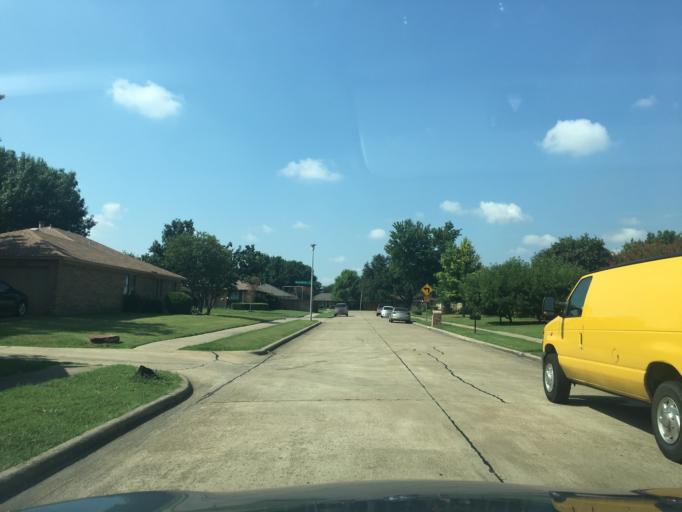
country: US
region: Texas
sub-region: Dallas County
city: Garland
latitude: 32.9498
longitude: -96.6288
